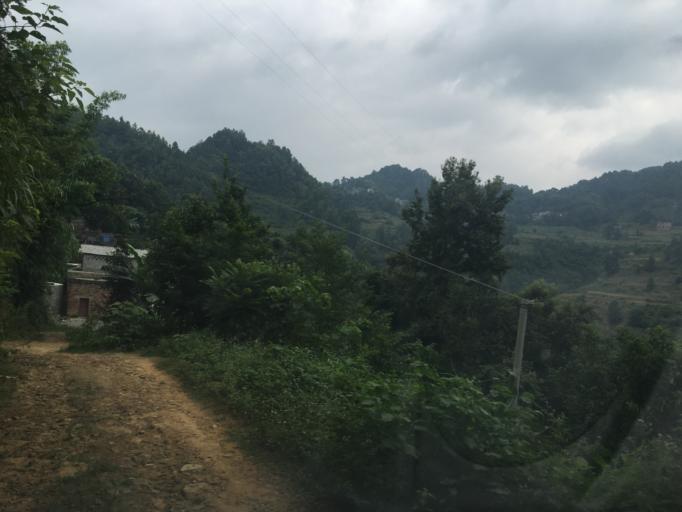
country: CN
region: Guangxi Zhuangzu Zizhiqu
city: Xinzhou
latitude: 25.1636
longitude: 105.6989
